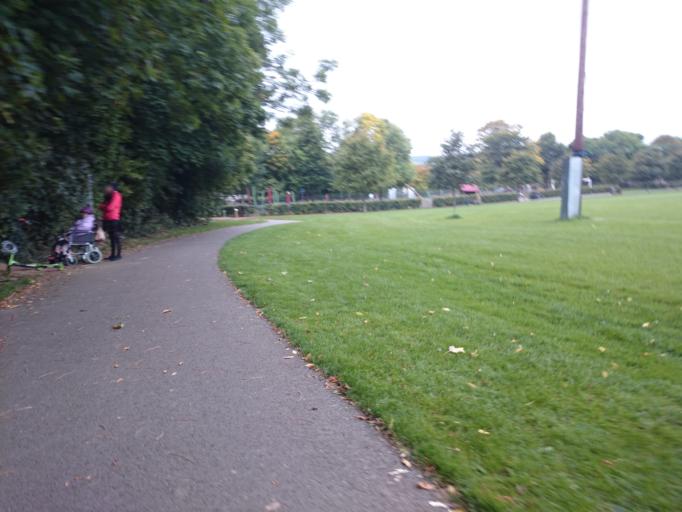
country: IE
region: Leinster
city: Shankill
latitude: 53.2222
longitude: -6.1206
